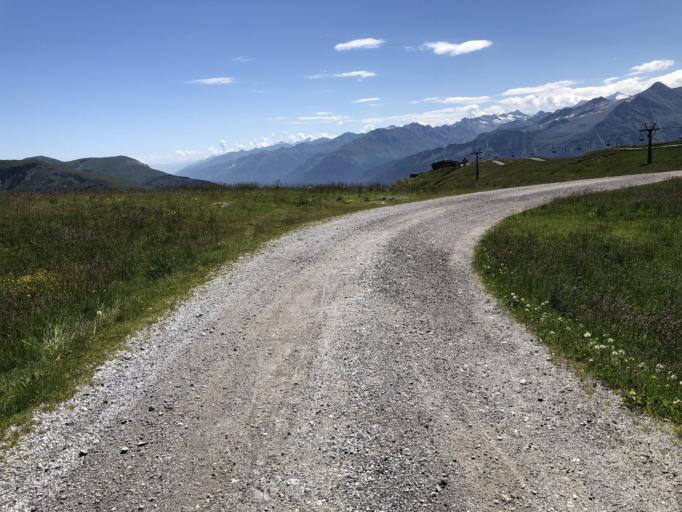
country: AT
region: Salzburg
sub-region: Politischer Bezirk Zell am See
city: Krimml
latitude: 47.2601
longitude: 12.0952
